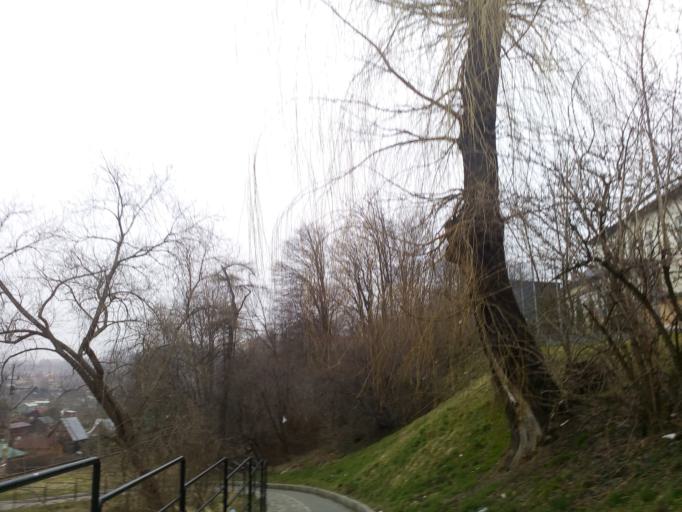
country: PL
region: Lesser Poland Voivodeship
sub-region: Powiat nowosadecki
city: Nowy Sacz
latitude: 49.6143
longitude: 20.6942
